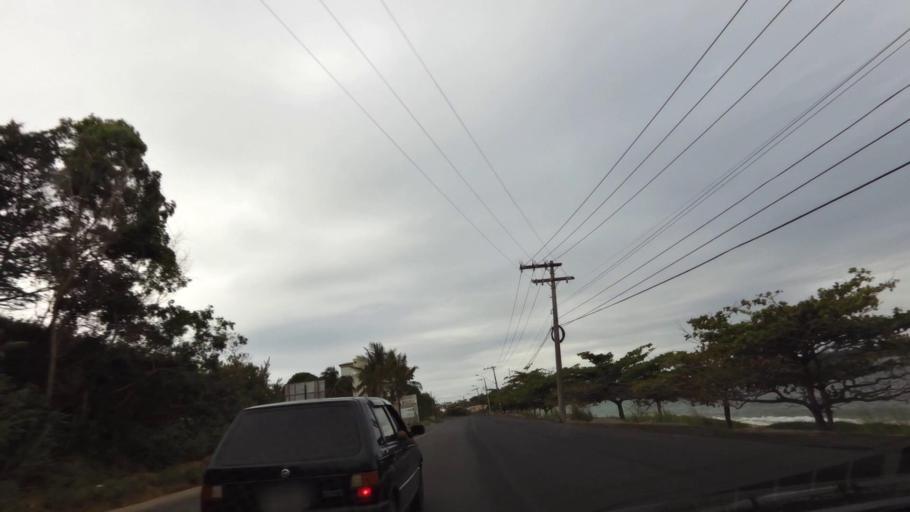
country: BR
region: Espirito Santo
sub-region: Guarapari
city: Guarapari
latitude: -20.7391
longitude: -40.5466
